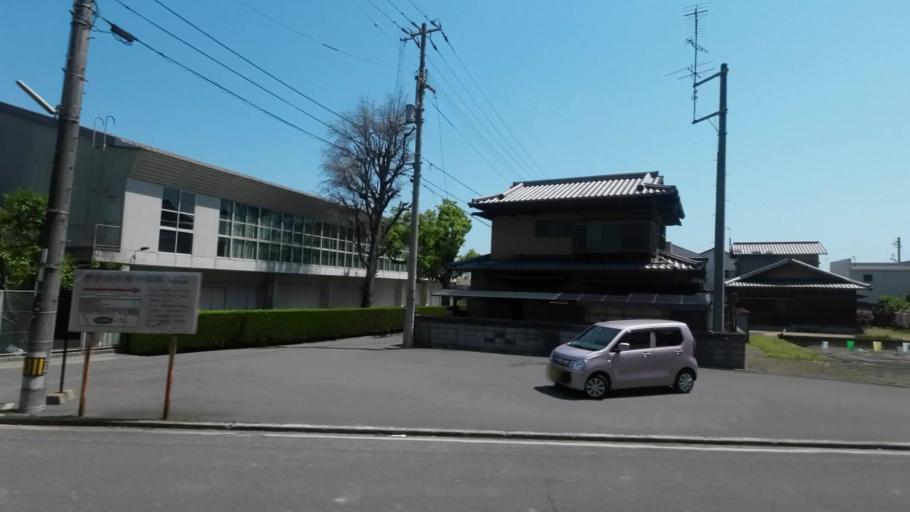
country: JP
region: Ehime
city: Saijo
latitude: 34.0157
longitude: 133.0337
